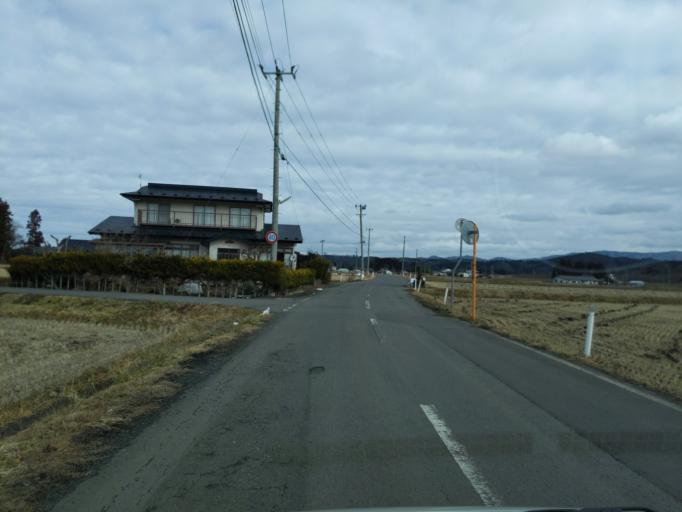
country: JP
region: Iwate
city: Mizusawa
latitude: 39.0890
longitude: 141.1744
